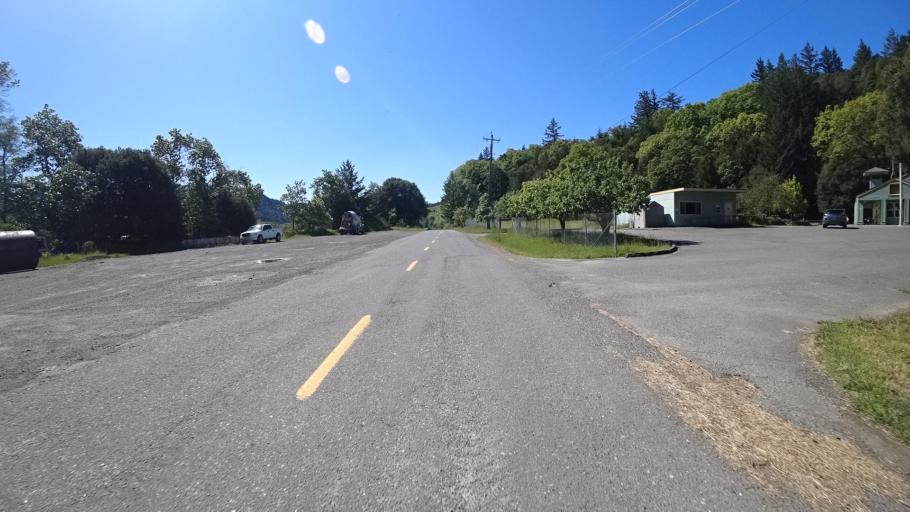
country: US
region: California
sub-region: Humboldt County
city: Rio Dell
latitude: 40.2426
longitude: -124.1229
